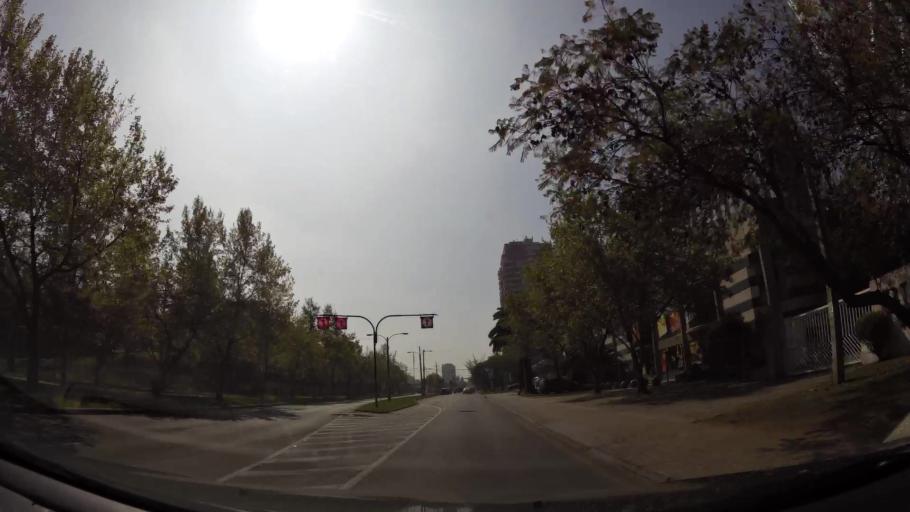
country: CL
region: Santiago Metropolitan
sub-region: Provincia de Santiago
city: Villa Presidente Frei, Nunoa, Santiago, Chile
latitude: -33.4030
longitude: -70.5711
